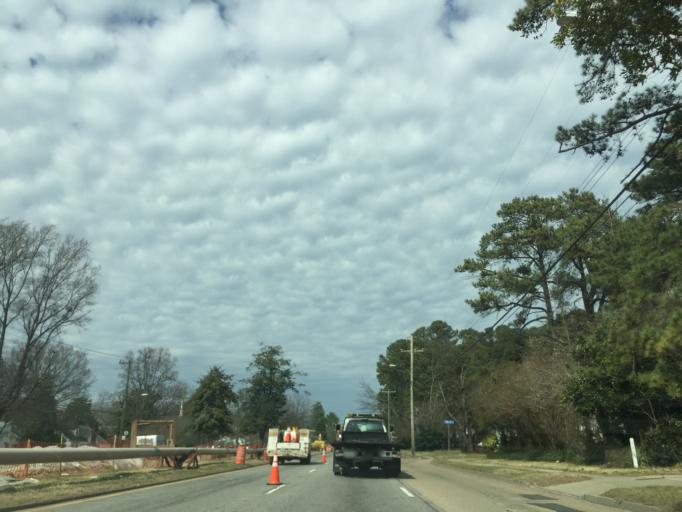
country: US
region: Virginia
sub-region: City of Norfolk
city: Norfolk
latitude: 36.8938
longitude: -76.2789
